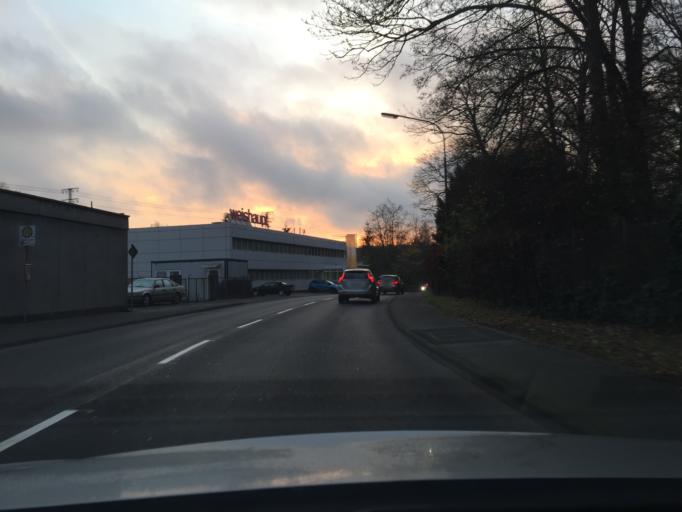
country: DE
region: Rheinland-Pfalz
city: Koblenz
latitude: 50.3768
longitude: 7.5897
